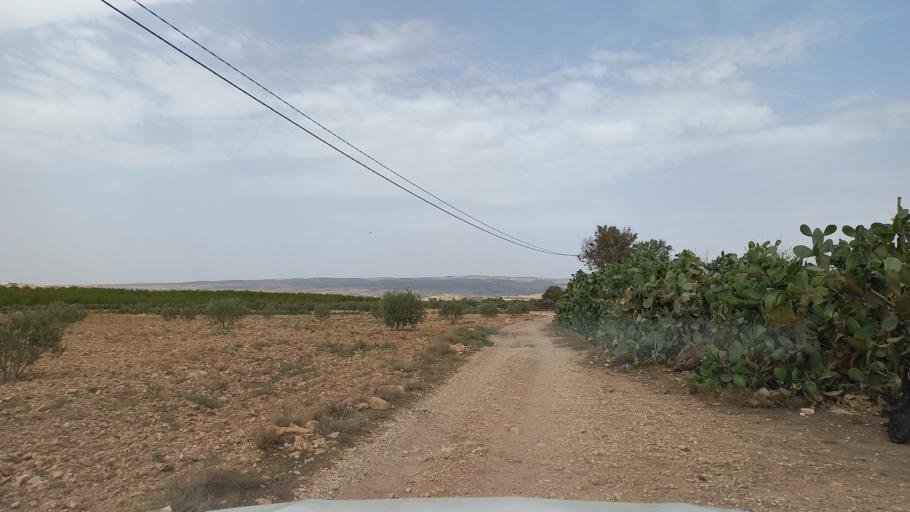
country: TN
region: Al Qasrayn
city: Kasserine
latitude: 35.2868
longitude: 9.0085
